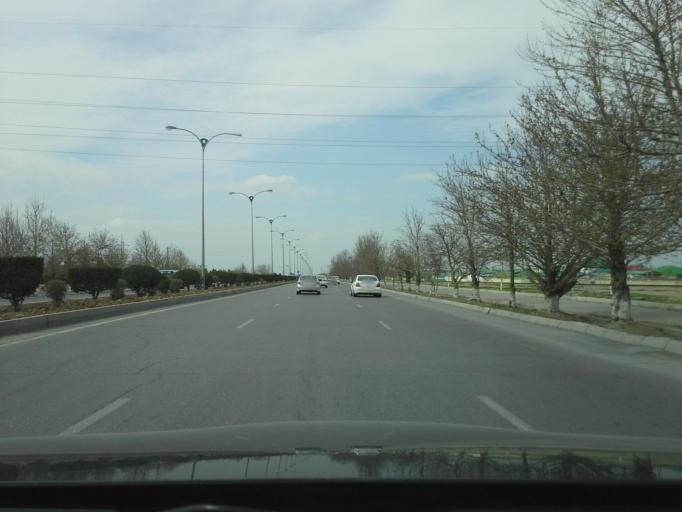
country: TM
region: Ahal
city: Abadan
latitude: 38.0638
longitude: 58.1662
